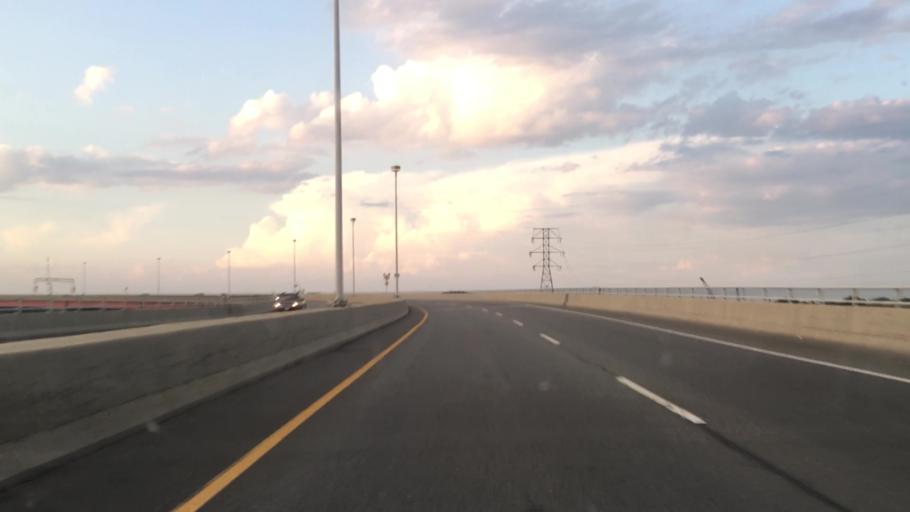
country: US
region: Maine
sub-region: Cumberland County
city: South Portland
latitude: 43.6405
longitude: -70.2578
